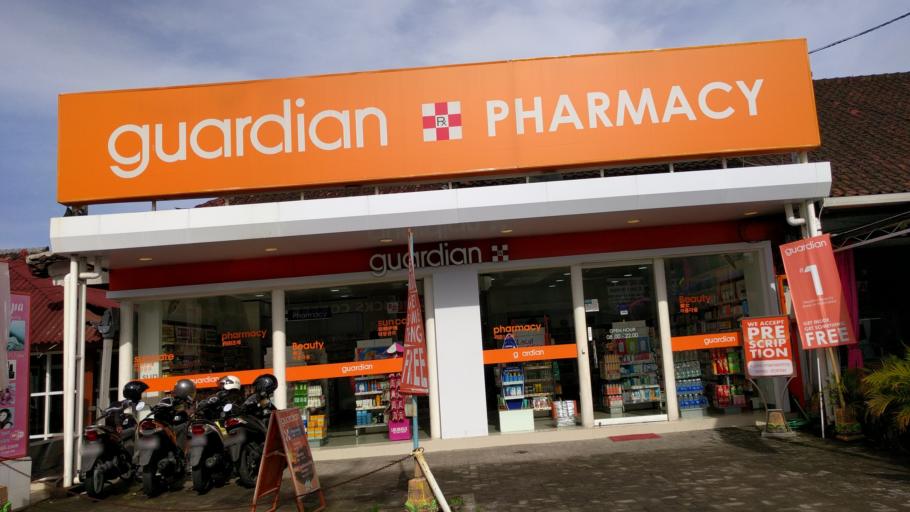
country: ID
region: Bali
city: Kuta
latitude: -8.6840
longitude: 115.1572
